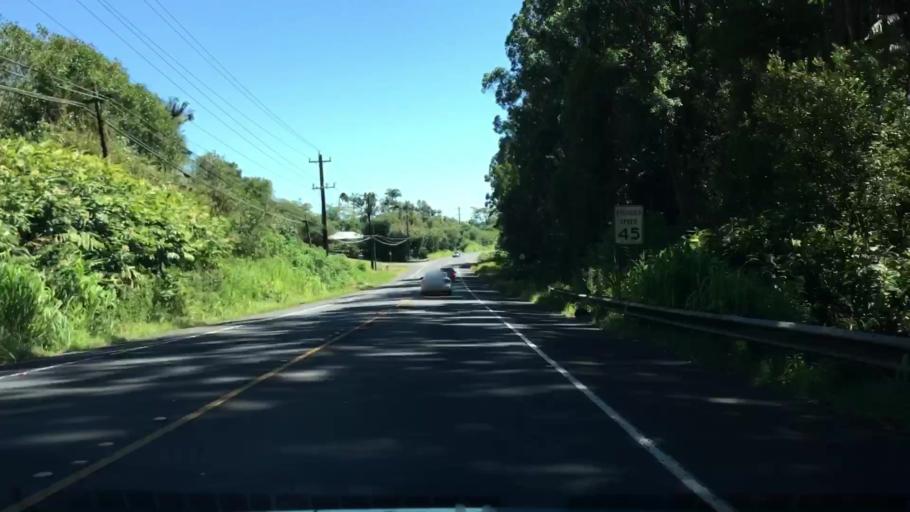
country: US
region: Hawaii
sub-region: Hawaii County
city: Mountain View
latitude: 19.5461
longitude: -155.1136
